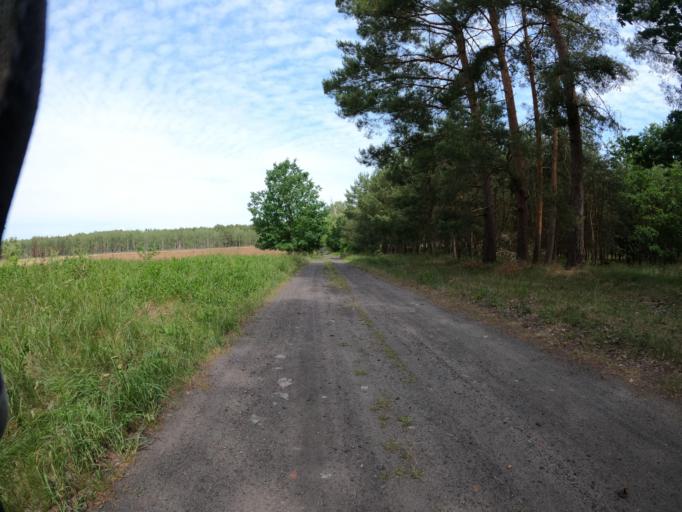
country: DE
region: Brandenburg
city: Zechin
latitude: 52.6790
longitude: 14.4880
